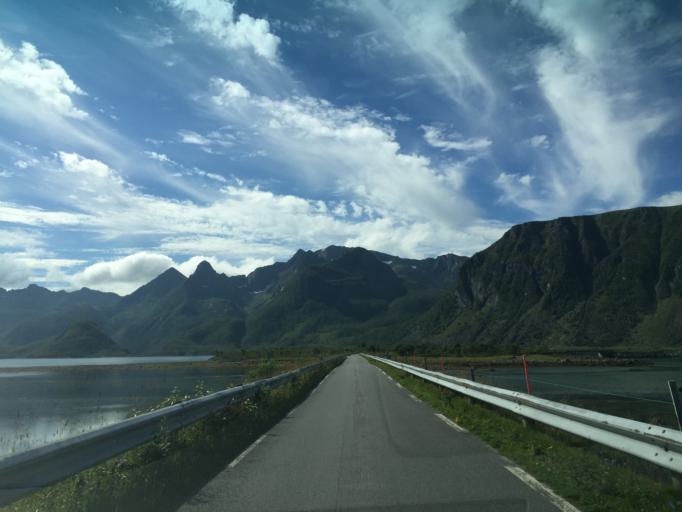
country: NO
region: Nordland
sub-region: Vagan
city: Svolvaer
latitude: 68.3973
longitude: 14.5653
